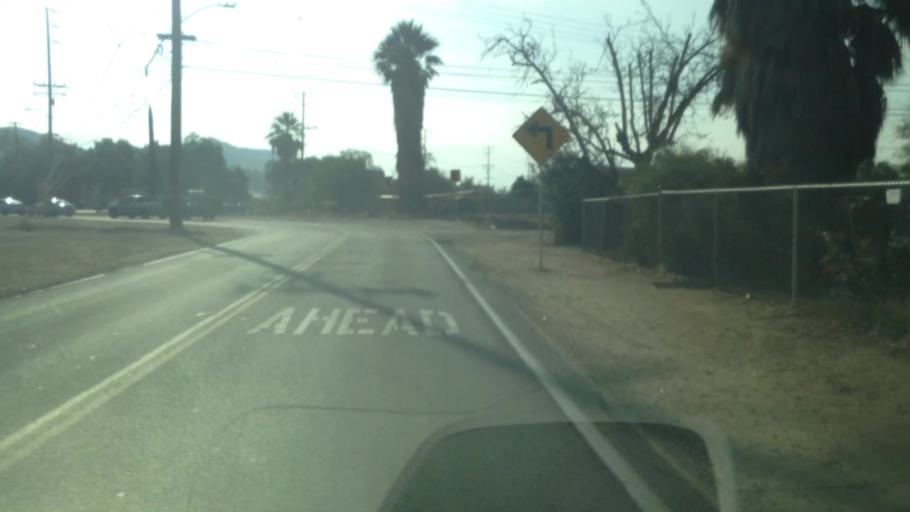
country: US
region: California
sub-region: Riverside County
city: Sunnyslope
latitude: 34.0088
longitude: -117.4392
